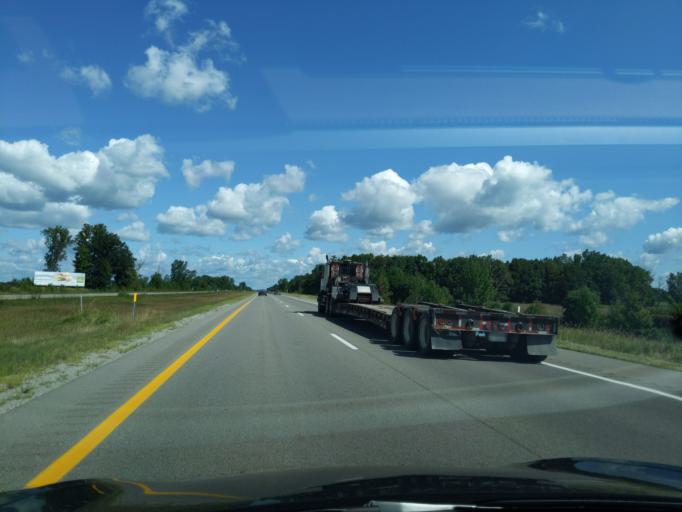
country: US
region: Michigan
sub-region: Isabella County
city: Shepherd
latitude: 43.4530
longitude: -84.6772
